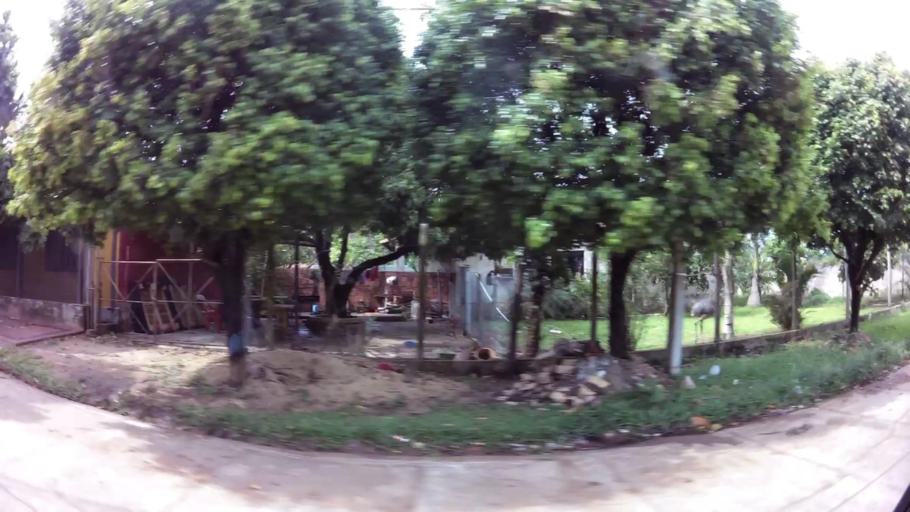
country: PY
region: Central
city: Limpio
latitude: -25.1741
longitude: -57.4723
